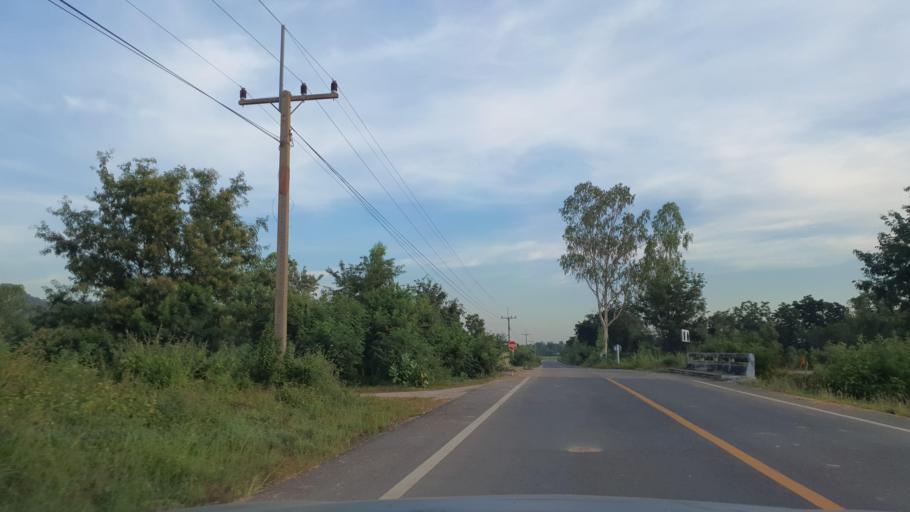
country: TH
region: Uthai Thani
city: Sawang Arom
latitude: 15.7179
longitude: 99.9531
